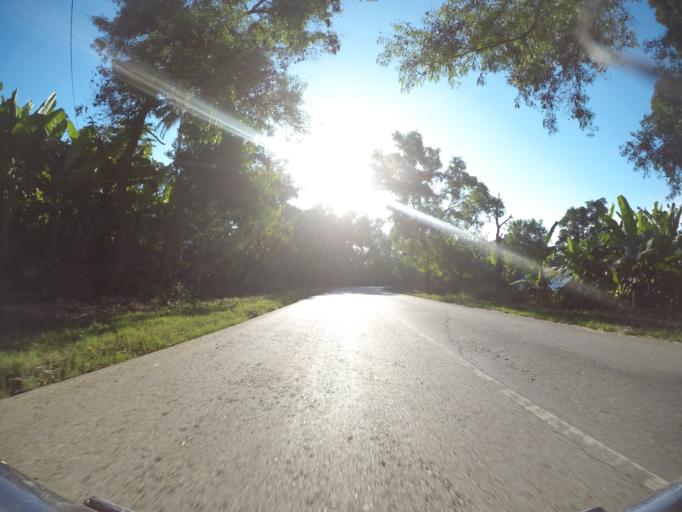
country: TZ
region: Pemba South
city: Uwelini
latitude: -5.3786
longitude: 39.6766
